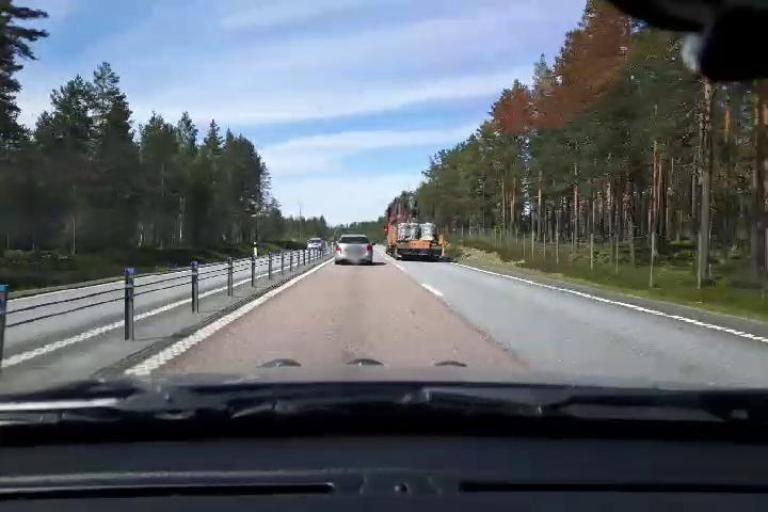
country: SE
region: Gaevleborg
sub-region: Gavle Kommun
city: Norrsundet
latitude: 61.0255
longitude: 16.9758
